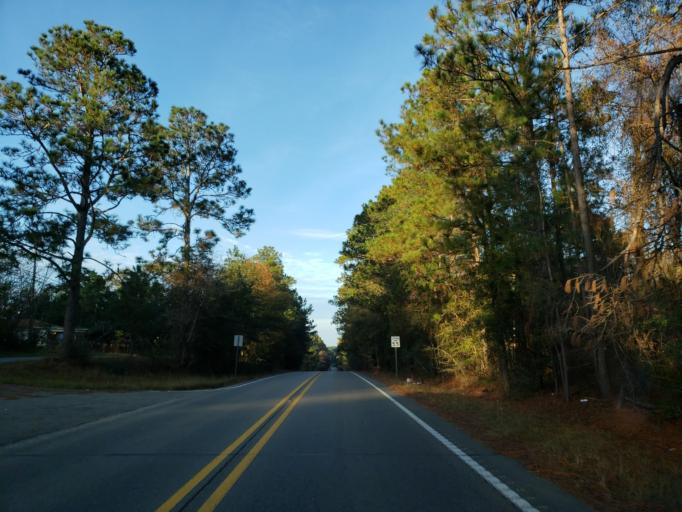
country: US
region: Mississippi
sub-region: Lamar County
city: Purvis
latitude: 31.1569
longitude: -89.3968
